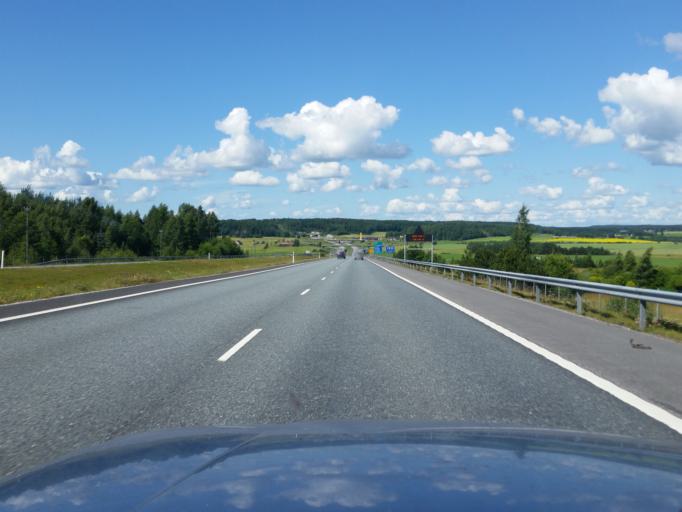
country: FI
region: Varsinais-Suomi
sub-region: Salo
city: Salo
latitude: 60.4114
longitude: 23.1956
